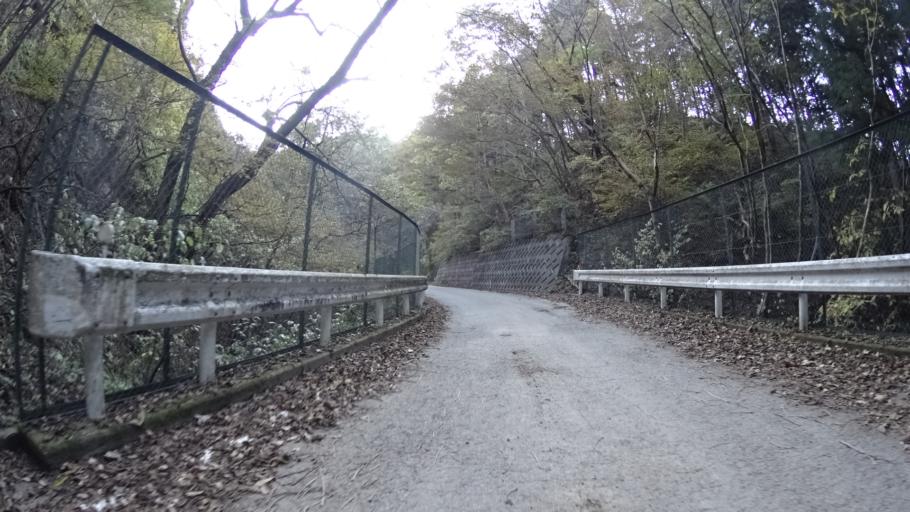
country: JP
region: Yamanashi
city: Uenohara
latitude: 35.6578
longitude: 139.1675
